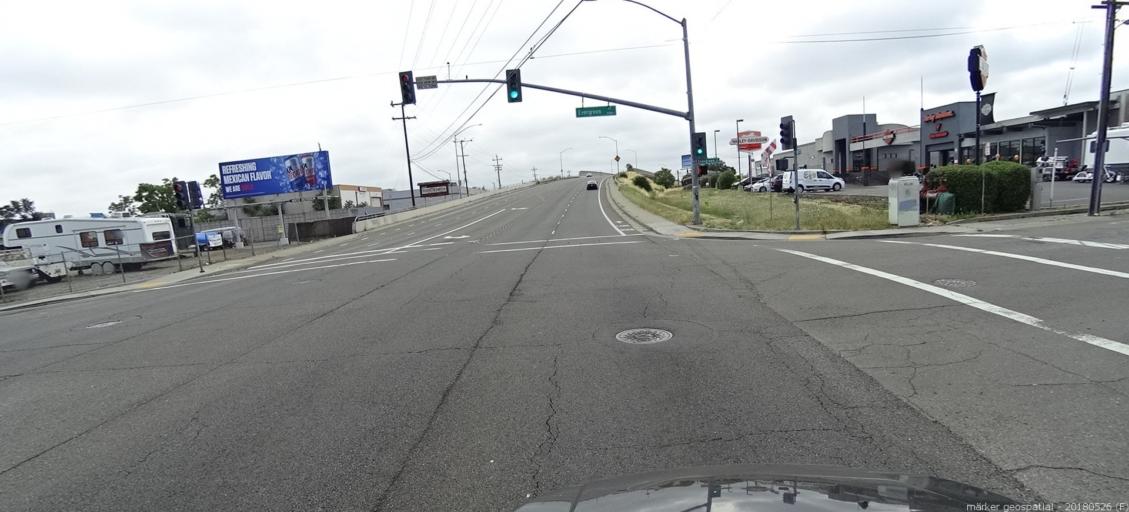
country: US
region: California
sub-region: Sacramento County
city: Sacramento
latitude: 38.6063
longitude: -121.4441
